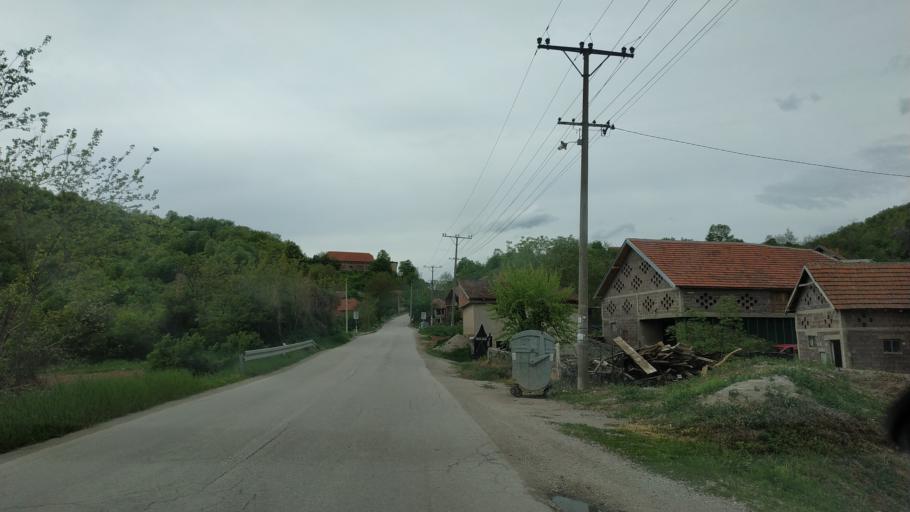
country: RS
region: Central Serbia
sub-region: Nisavski Okrug
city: Aleksinac
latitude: 43.6357
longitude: 21.7171
